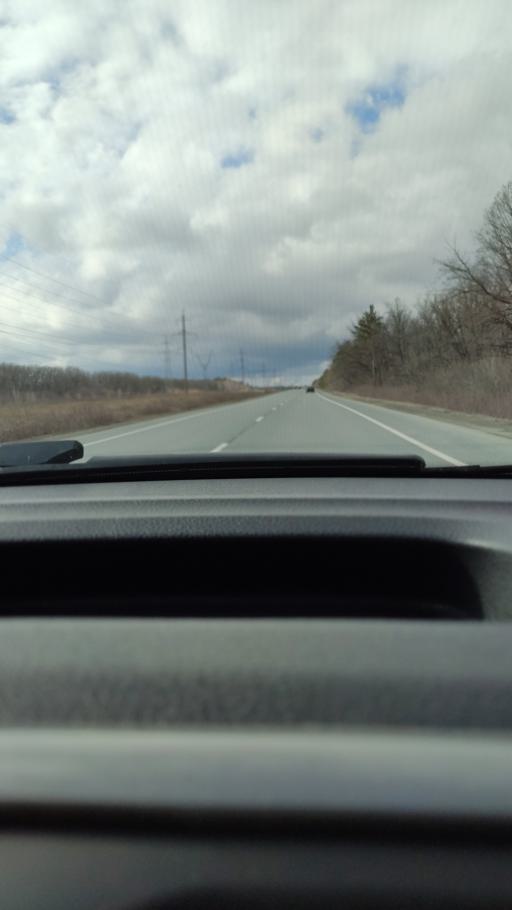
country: RU
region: Samara
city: Bogatyr'
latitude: 53.5006
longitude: 49.9514
